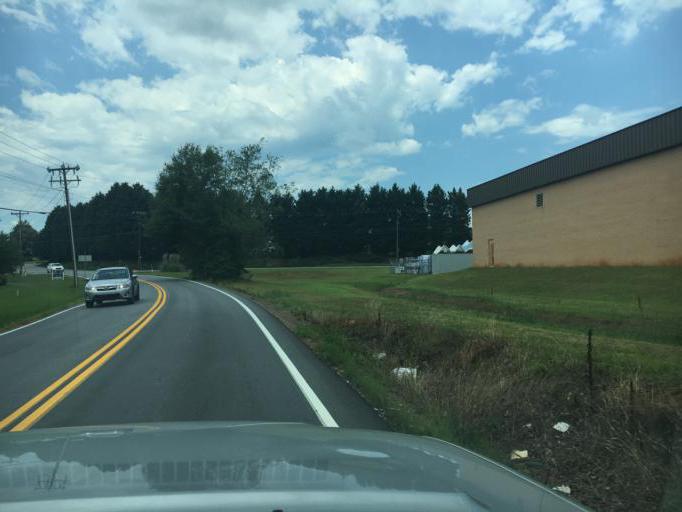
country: US
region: South Carolina
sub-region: Greenville County
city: Taylors
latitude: 34.8706
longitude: -82.2498
